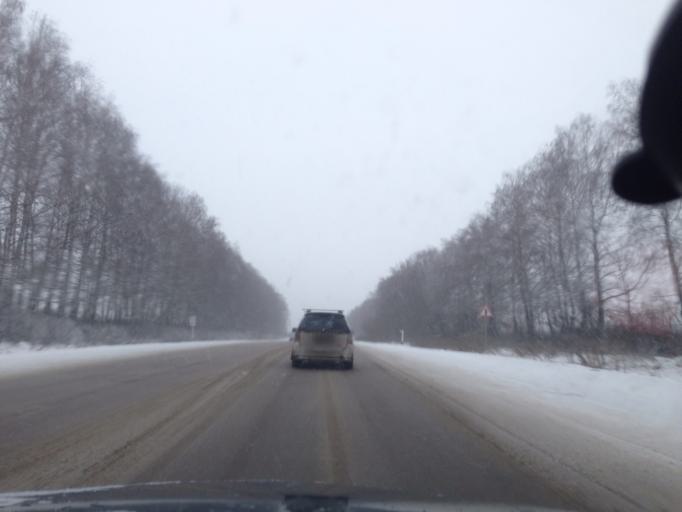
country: RU
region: Tula
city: Skuratovskiy
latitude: 54.1175
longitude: 37.7137
